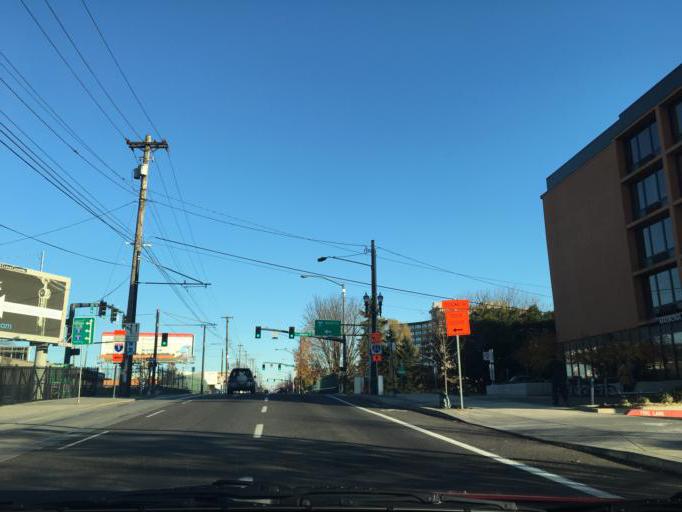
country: US
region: Oregon
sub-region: Multnomah County
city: Portland
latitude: 45.5344
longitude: -122.6674
